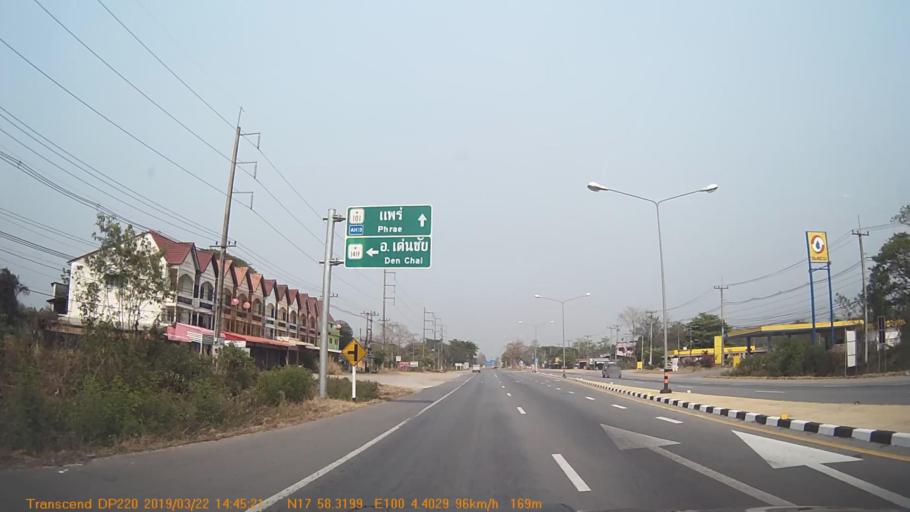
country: TH
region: Phrae
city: Den Chai
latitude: 17.9722
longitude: 100.0739
